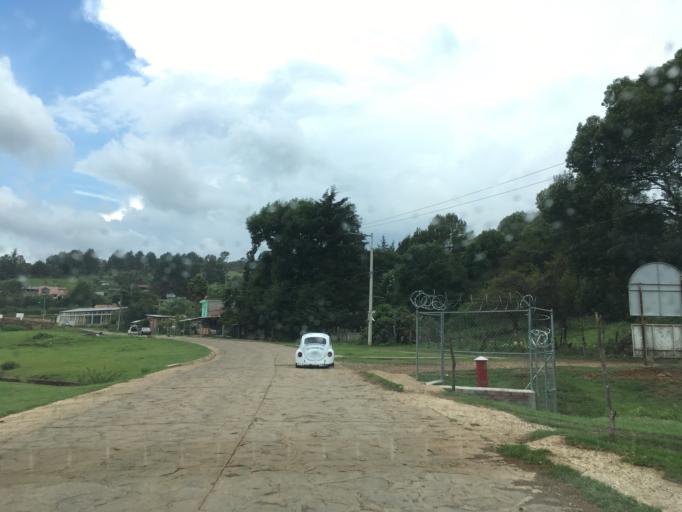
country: MX
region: Michoacan
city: Acuitzio del Canje
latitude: 19.5308
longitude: -101.2534
